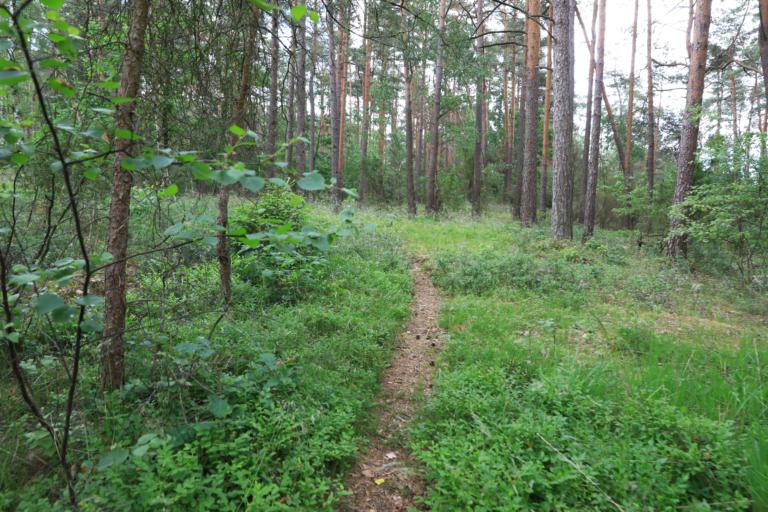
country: SE
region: Halland
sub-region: Varbergs Kommun
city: Varberg
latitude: 57.1725
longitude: 12.2583
